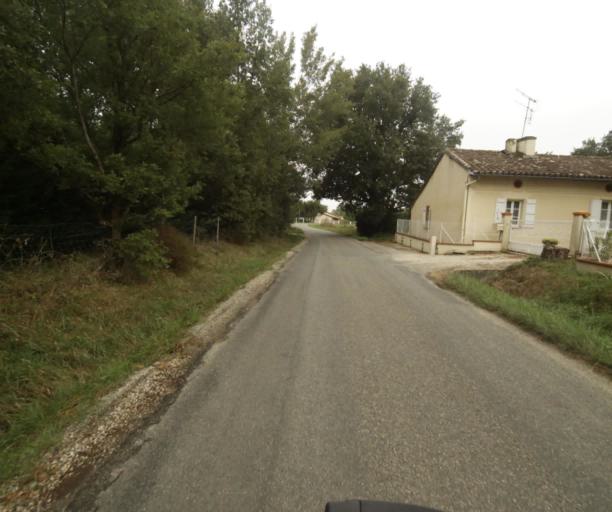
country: FR
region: Midi-Pyrenees
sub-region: Departement du Tarn-et-Garonne
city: Labastide-Saint-Pierre
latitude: 43.8864
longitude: 1.3807
